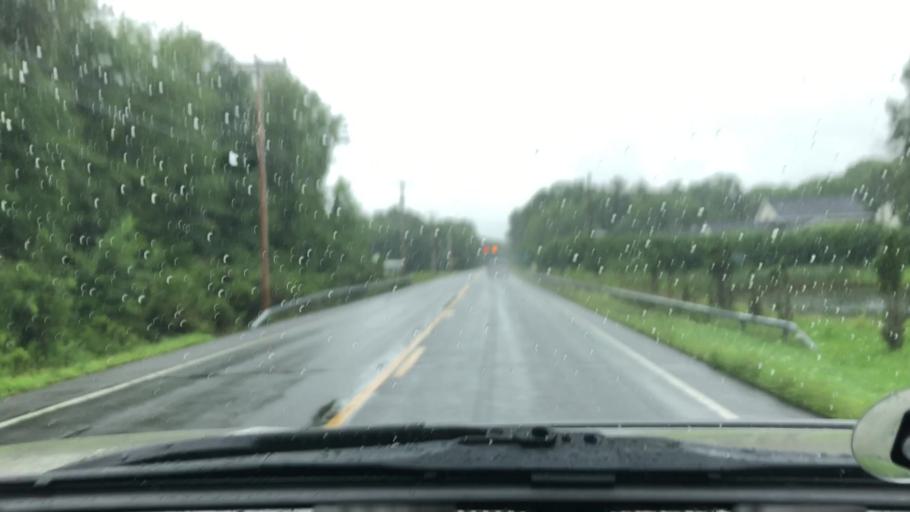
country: US
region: New York
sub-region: Greene County
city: Cairo
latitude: 42.2803
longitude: -73.9807
